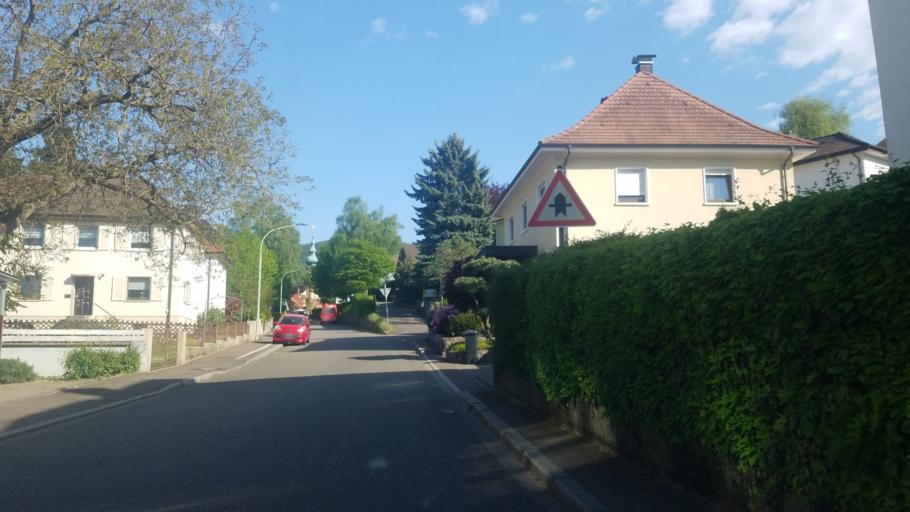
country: DE
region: Baden-Wuerttemberg
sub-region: Karlsruhe Region
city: Buhl
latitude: 48.6932
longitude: 8.1416
